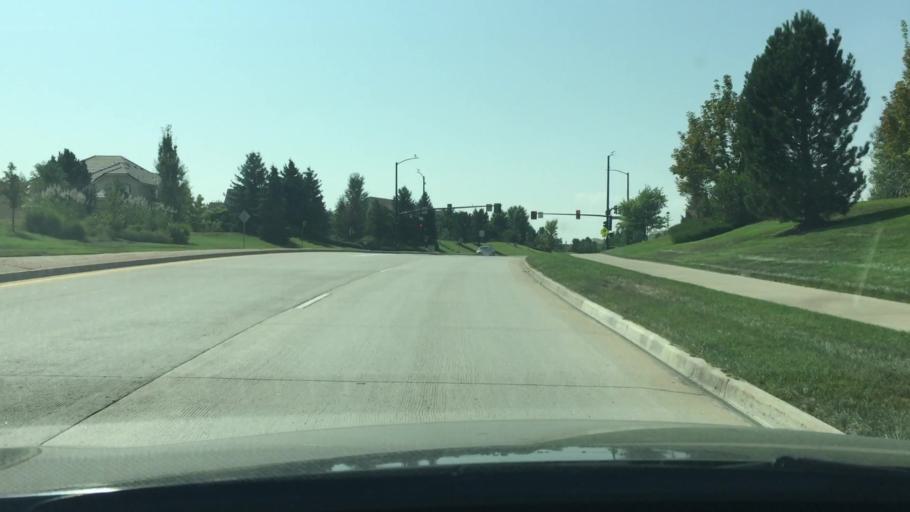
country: US
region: Colorado
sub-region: Arapahoe County
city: Dove Valley
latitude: 39.6034
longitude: -104.7870
